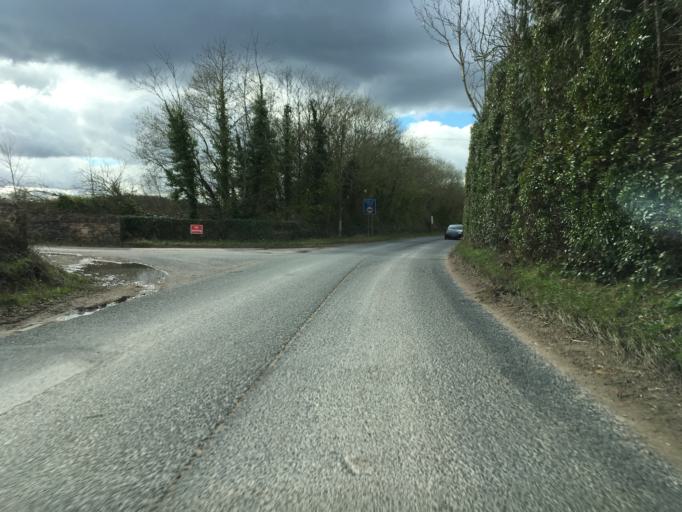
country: GB
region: England
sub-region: Gloucestershire
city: Coleford
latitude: 51.7576
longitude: -2.6292
